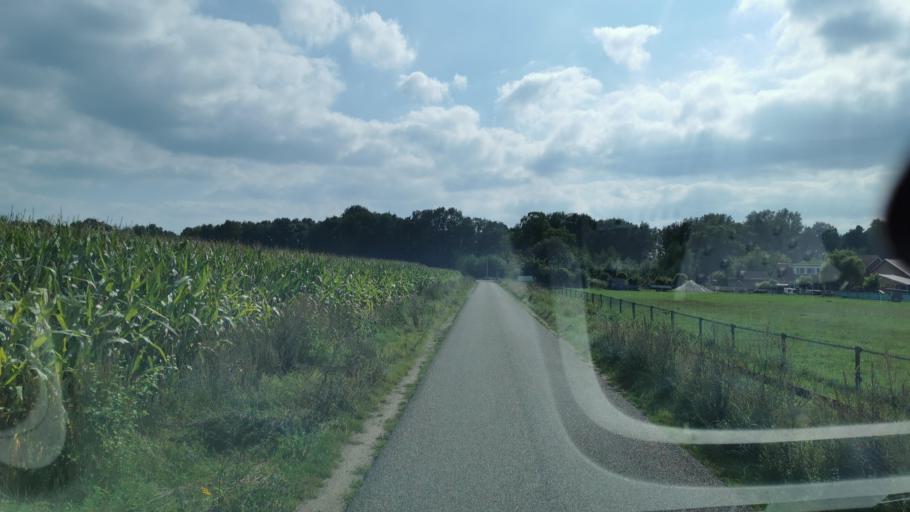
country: NL
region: Overijssel
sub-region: Gemeente Hengelo
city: Hengelo
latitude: 52.3260
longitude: 6.8411
